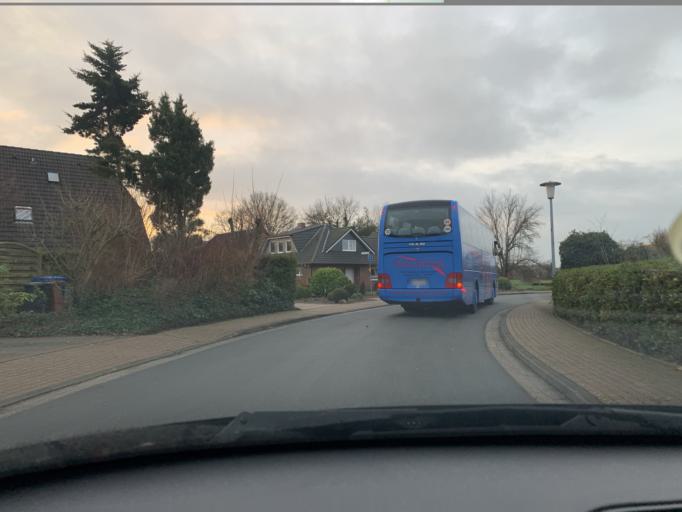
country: DE
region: Lower Saxony
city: Westerstede
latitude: 53.2514
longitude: 7.9065
